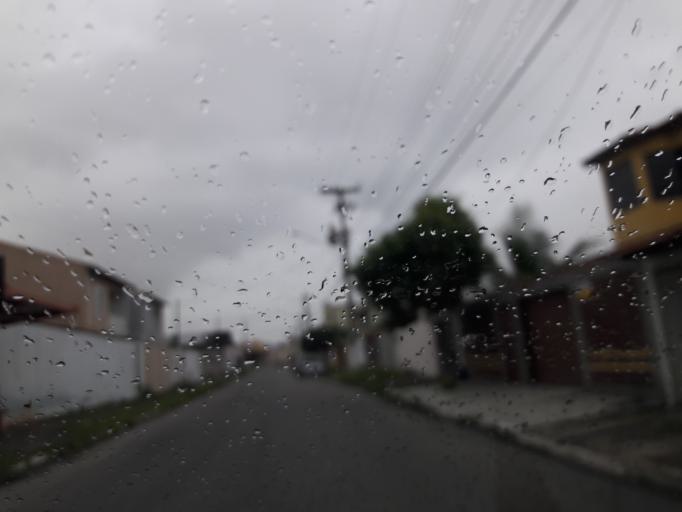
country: BR
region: Rio de Janeiro
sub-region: Resende
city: Resende
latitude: -22.4855
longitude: -44.5021
